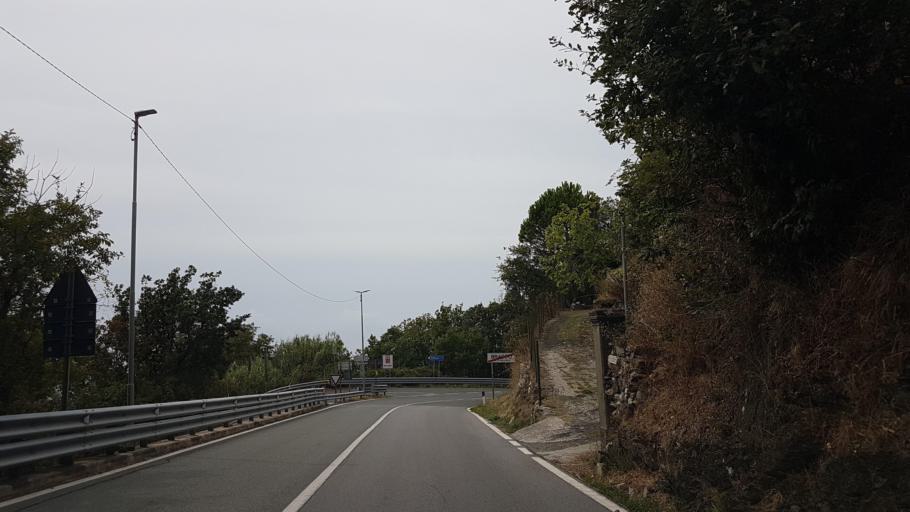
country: IT
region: Liguria
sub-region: Provincia di Genova
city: Moneglia
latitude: 44.2572
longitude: 9.5023
